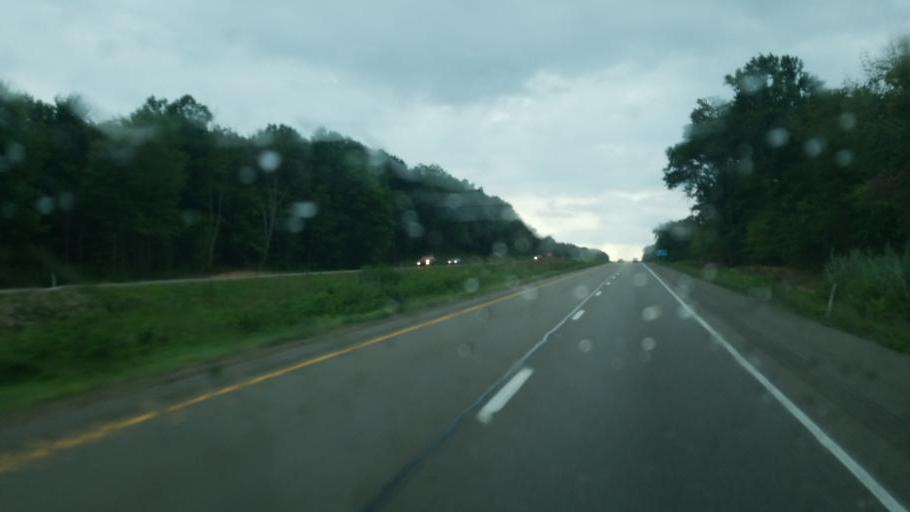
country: US
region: Pennsylvania
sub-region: Mercer County
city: Grove City
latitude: 41.1737
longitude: -80.1668
